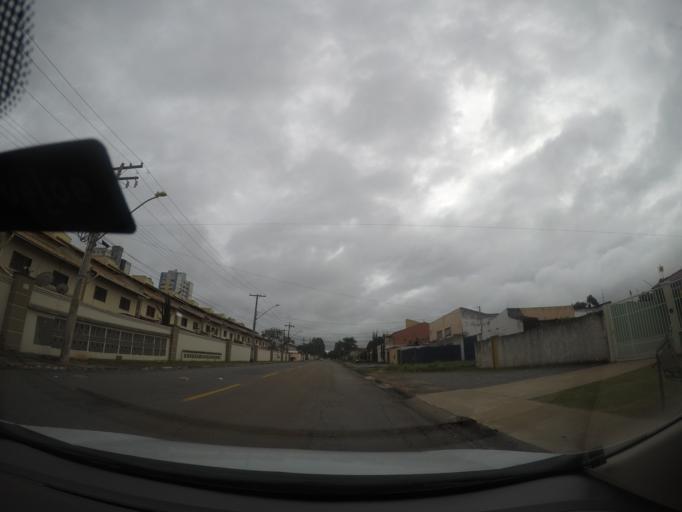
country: BR
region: Goias
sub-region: Goiania
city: Goiania
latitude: -16.7220
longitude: -49.2928
